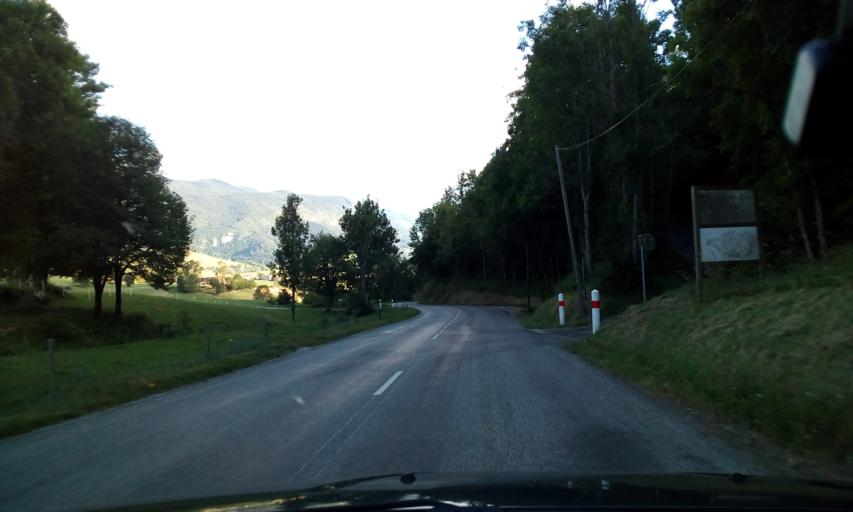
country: FR
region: Rhone-Alpes
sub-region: Departement de l'Isere
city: Pont-en-Royans
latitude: 45.0334
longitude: 5.4439
